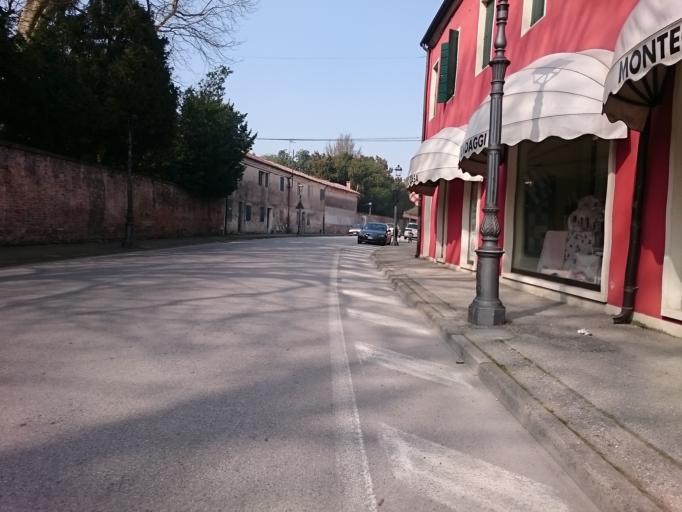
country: IT
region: Veneto
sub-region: Provincia di Padova
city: Pernumia
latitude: 45.2566
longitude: 11.7904
